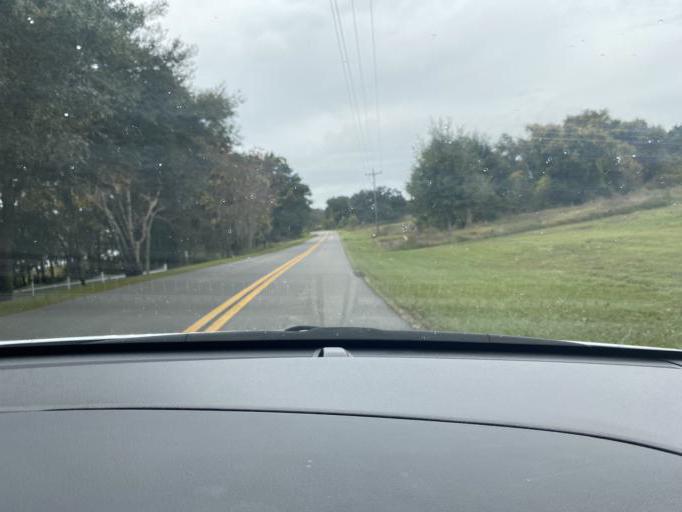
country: US
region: Florida
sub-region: Lake County
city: Groveland
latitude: 28.6026
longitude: -81.8078
